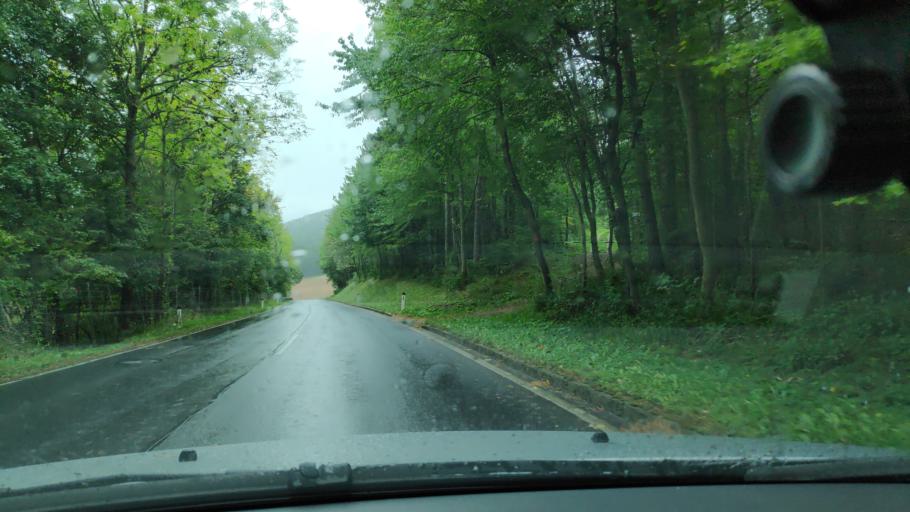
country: AT
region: Lower Austria
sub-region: Politischer Bezirk Neunkirchen
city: Grunbach am Schneeberg
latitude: 47.7916
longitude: 16.0116
